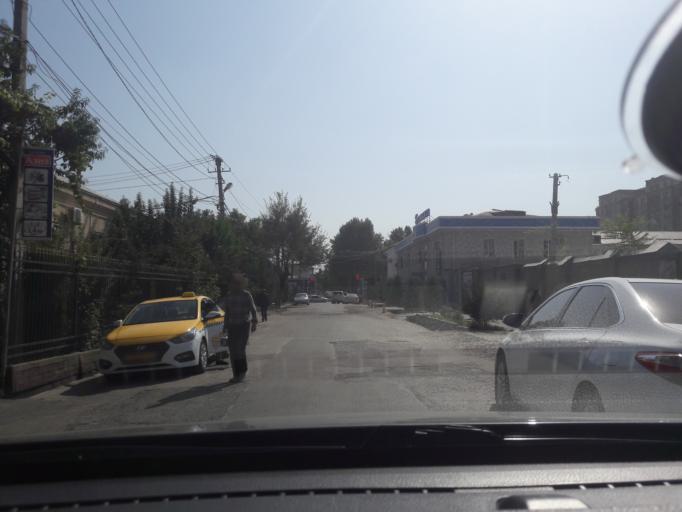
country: TJ
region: Dushanbe
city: Dushanbe
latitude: 38.5641
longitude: 68.8047
